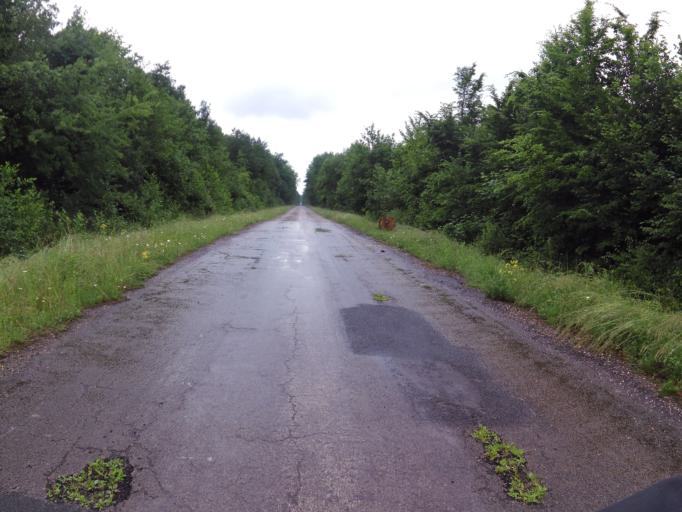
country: FR
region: Champagne-Ardenne
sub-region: Departement de la Marne
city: Sermaize-les-Bains
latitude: 48.7555
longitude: 4.9561
